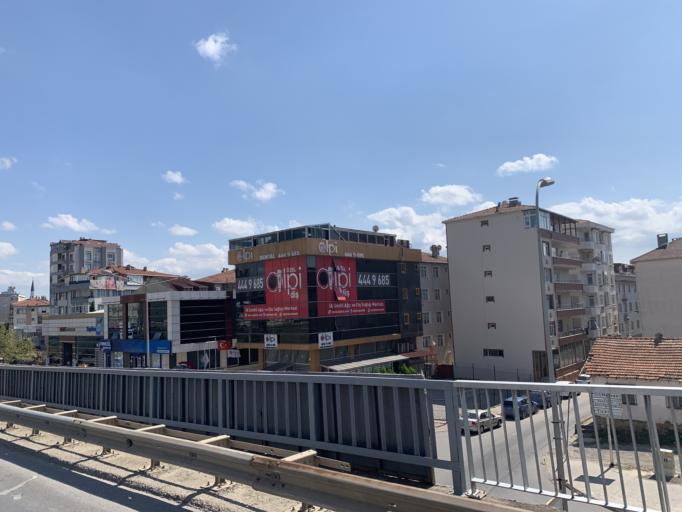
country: TR
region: Istanbul
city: Pendik
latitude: 40.8798
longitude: 29.2575
